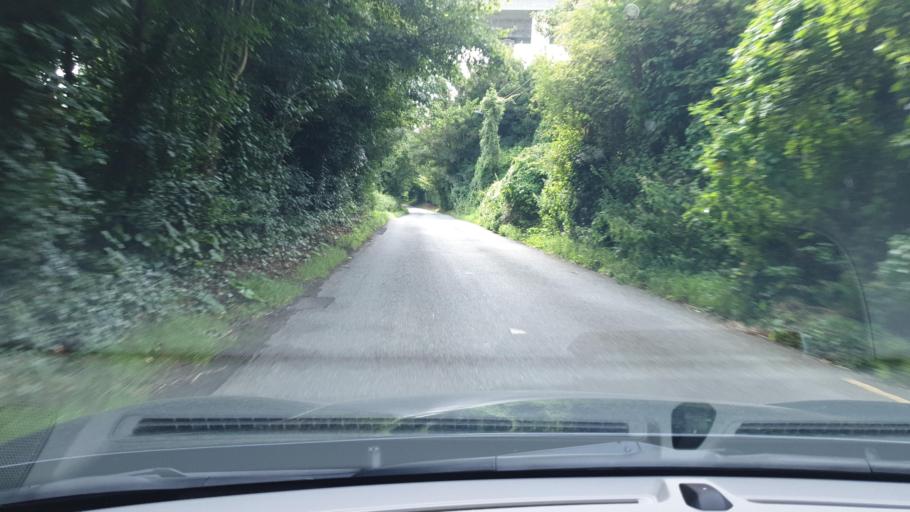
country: IE
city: Palmerstown
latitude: 53.3629
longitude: -6.3802
